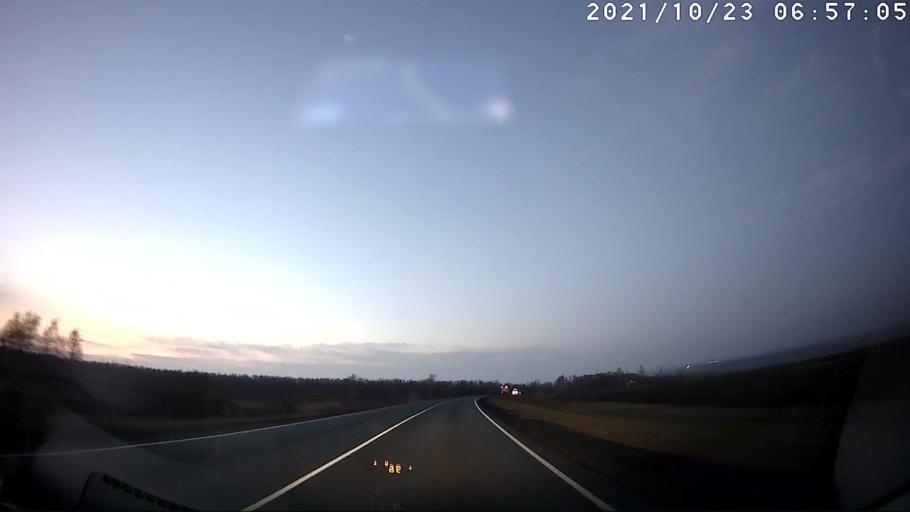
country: RU
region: Saratov
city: Dukhovnitskoye
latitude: 52.7139
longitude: 48.2668
